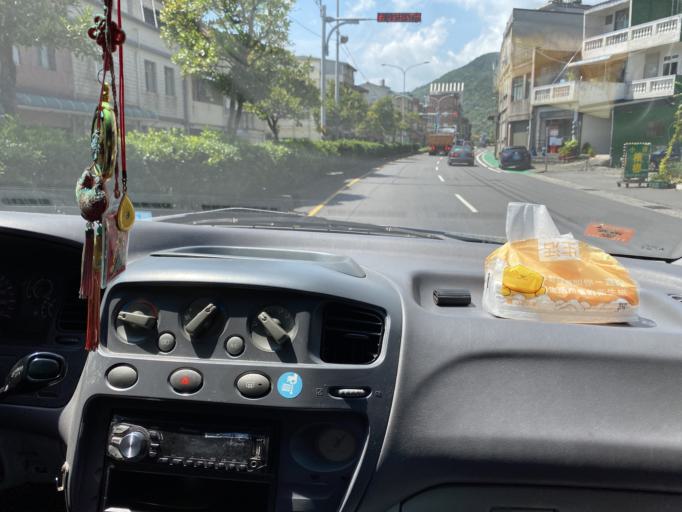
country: TW
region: Taiwan
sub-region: Yilan
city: Yilan
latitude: 24.9403
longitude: 121.8934
